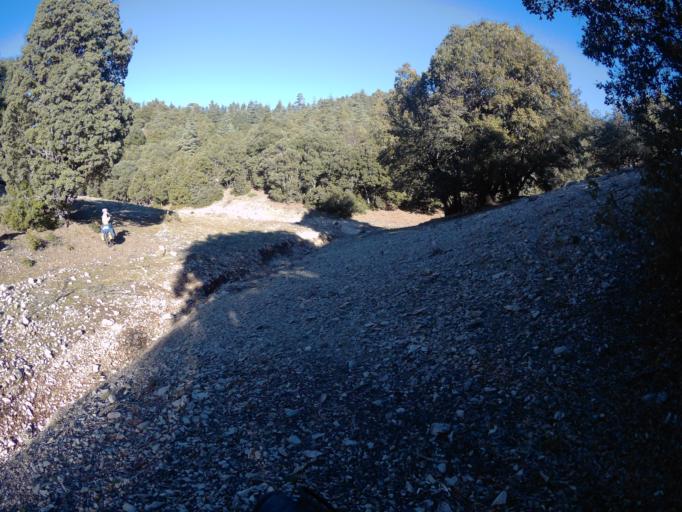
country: MA
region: Meknes-Tafilalet
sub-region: Ifrane
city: Azrou
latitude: 33.4168
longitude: -5.1282
